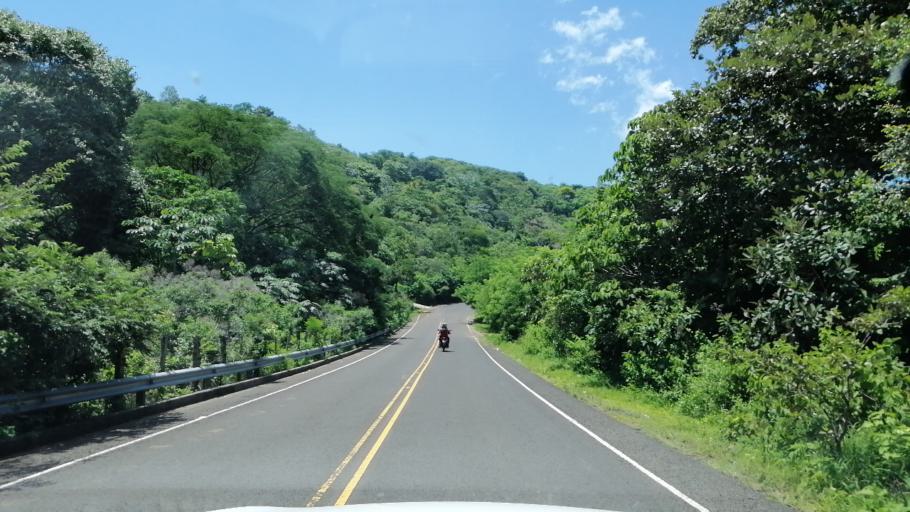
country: SV
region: San Miguel
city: Ciudad Barrios
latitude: 13.7962
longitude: -88.2935
